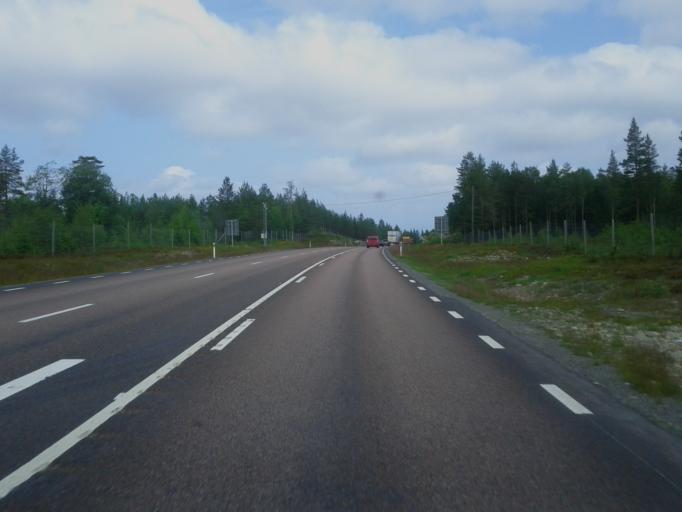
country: SE
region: Vaesterbotten
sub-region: Skelleftea Kommun
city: Burea
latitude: 64.4348
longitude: 21.2799
